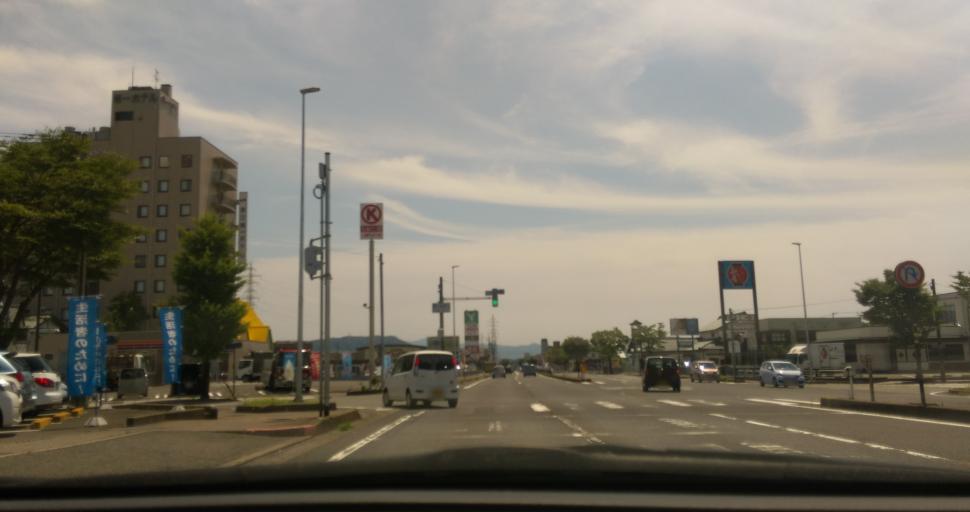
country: JP
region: Fukui
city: Sabae
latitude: 35.9434
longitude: 136.1939
